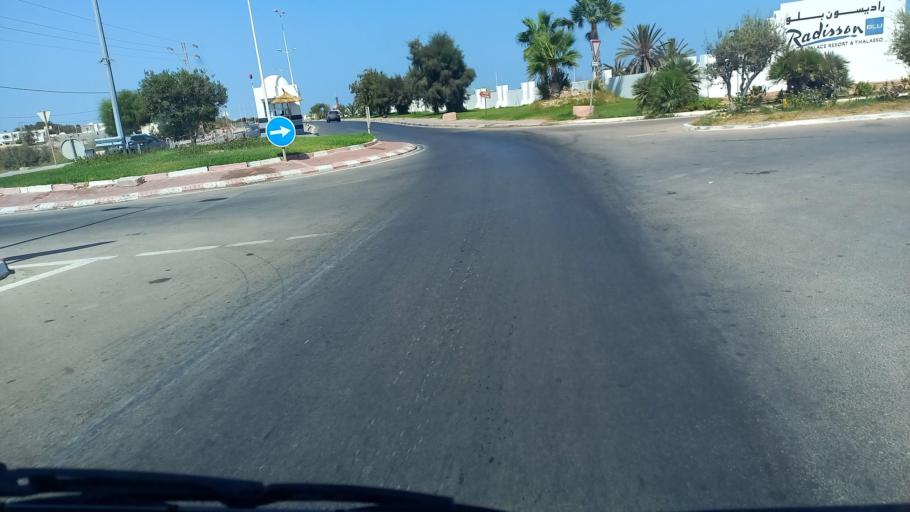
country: TN
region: Madanin
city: Midoun
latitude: 33.8687
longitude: 10.9576
